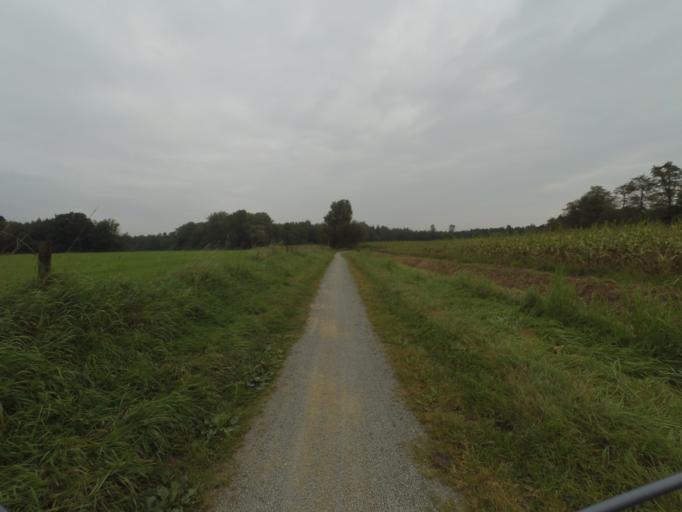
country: NL
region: Overijssel
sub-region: Gemeente Losser
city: Losser
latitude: 52.2828
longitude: 7.0300
